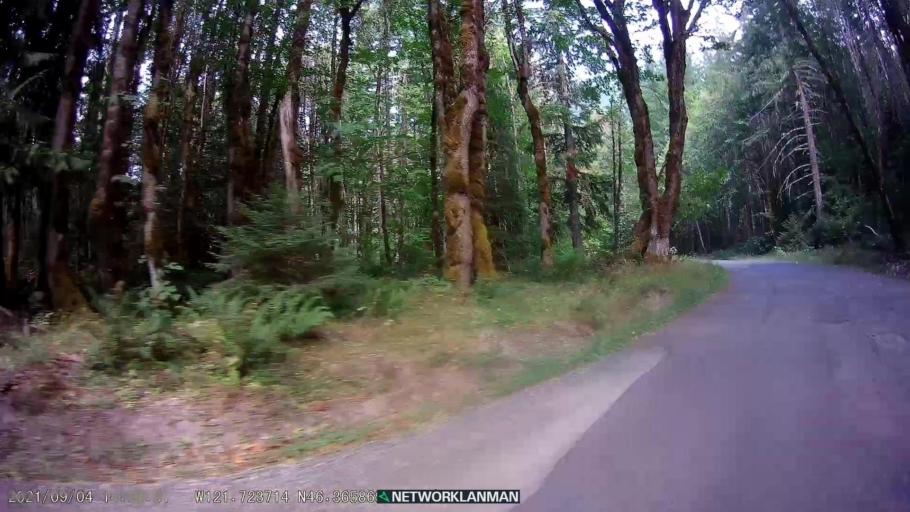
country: US
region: Washington
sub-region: Lewis County
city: Morton
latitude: 46.3660
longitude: -121.7239
